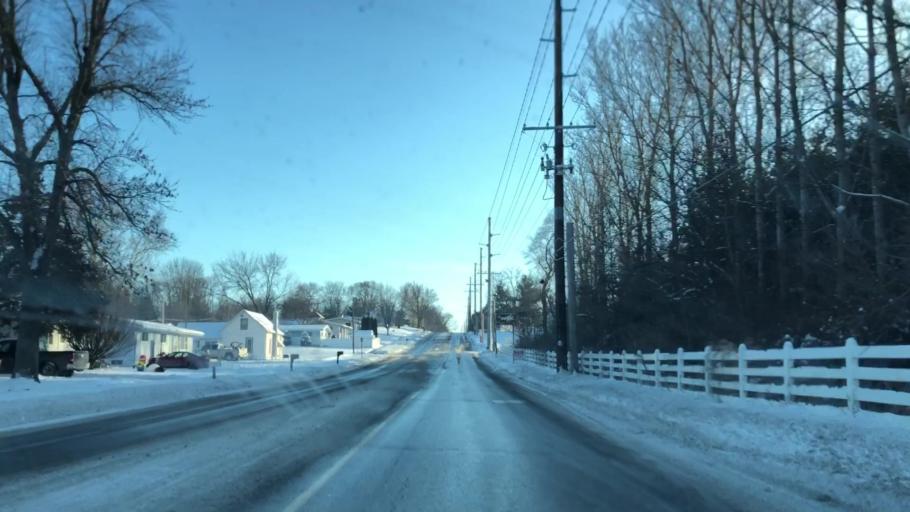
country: US
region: Iowa
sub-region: Marshall County
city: Marshalltown
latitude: 42.0357
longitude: -92.9224
